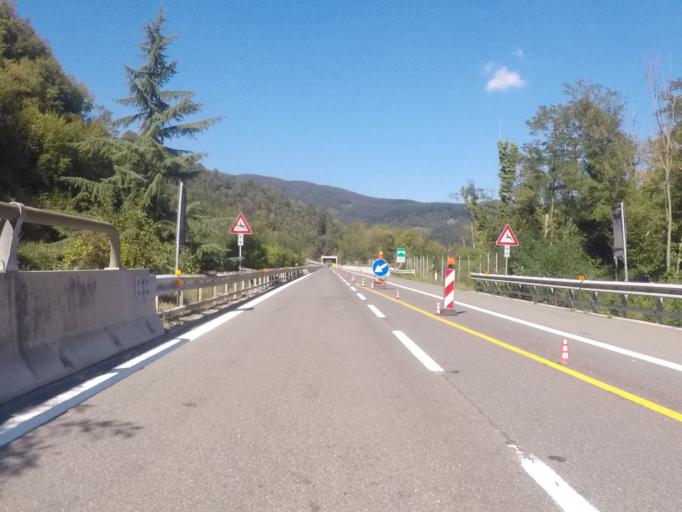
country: IT
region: Tuscany
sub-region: Provincia di Prato
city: Mercatale-San Quirico
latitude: 44.0645
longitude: 11.2090
